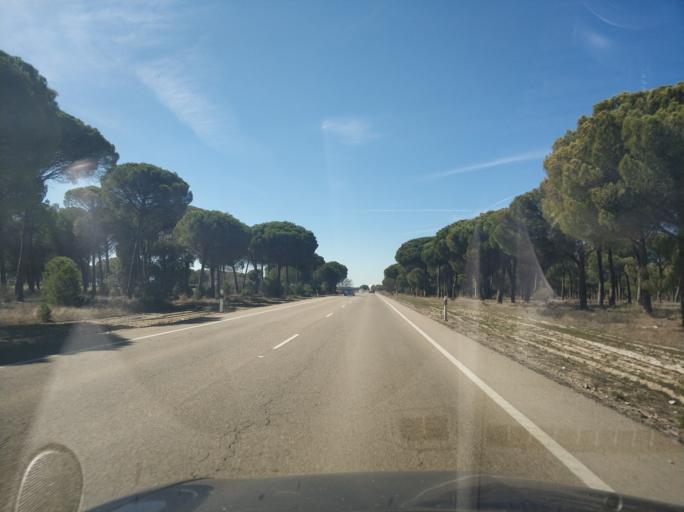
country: ES
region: Castille and Leon
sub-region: Provincia de Valladolid
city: Tudela de Duero
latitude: 41.5618
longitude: -4.6152
